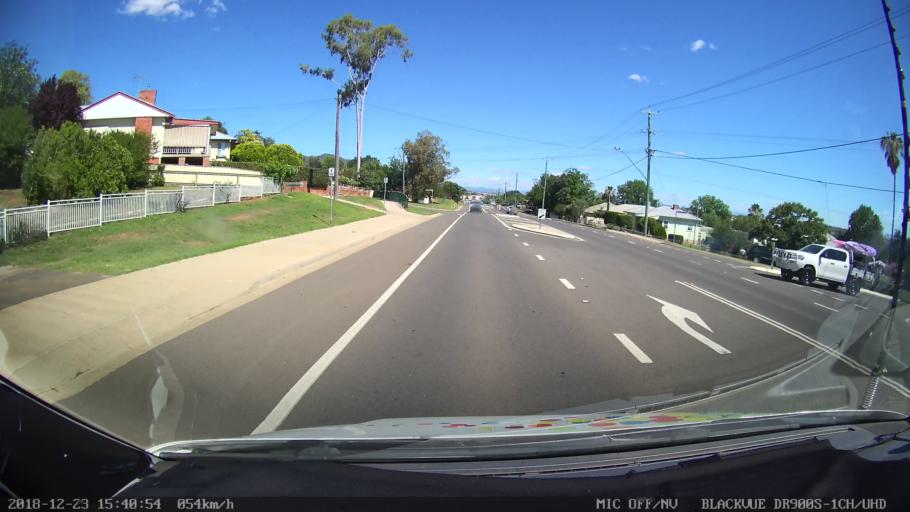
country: AU
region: New South Wales
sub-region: Tamworth Municipality
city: Tamworth
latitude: -31.0735
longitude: 150.9131
